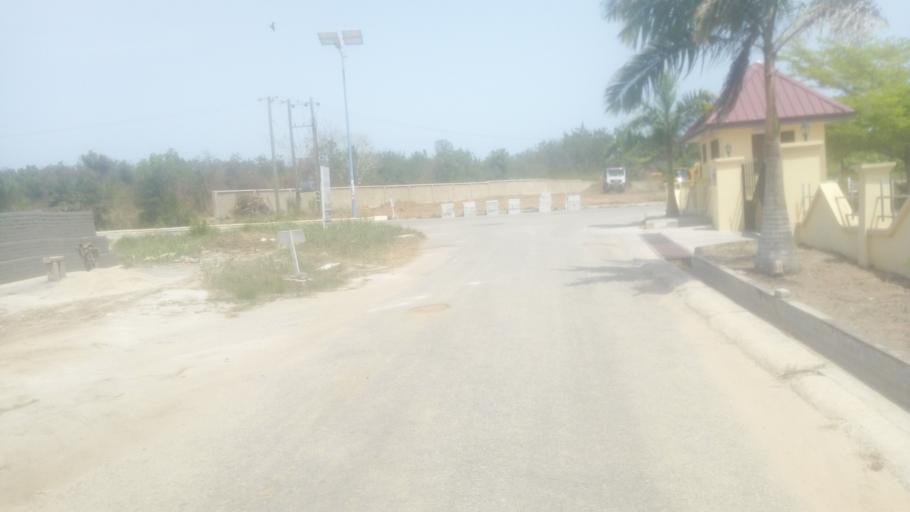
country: GH
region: Central
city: Winneba
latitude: 5.3684
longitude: -0.6291
